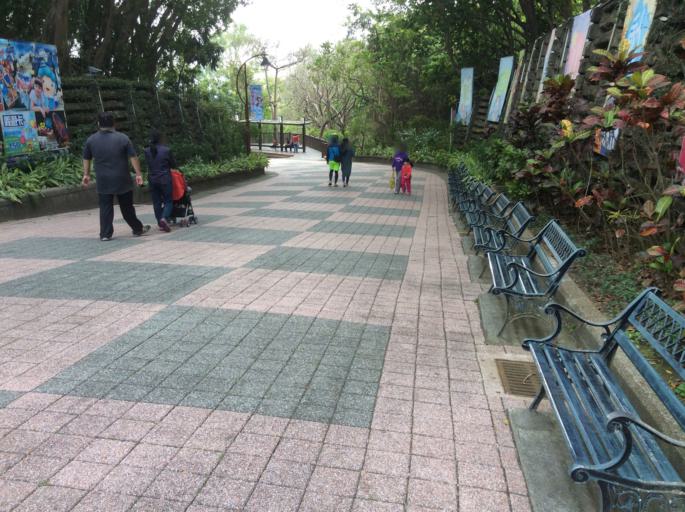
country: TW
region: Kaohsiung
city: Kaohsiung
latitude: 22.6344
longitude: 120.2753
